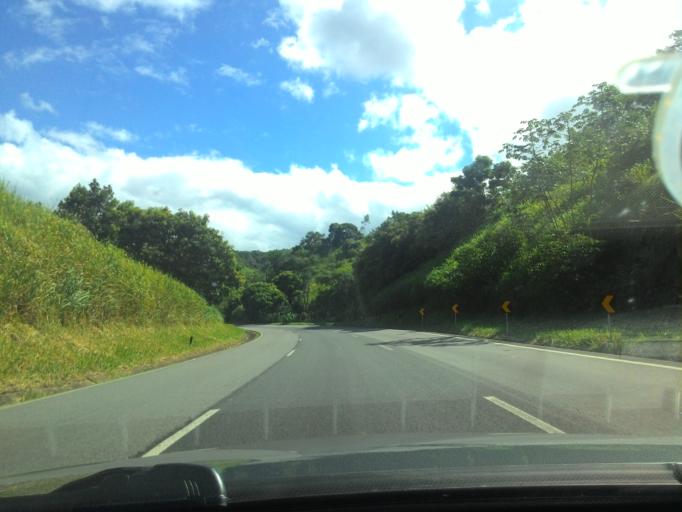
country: BR
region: Sao Paulo
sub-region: Cajati
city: Cajati
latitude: -24.8057
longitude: -48.2152
